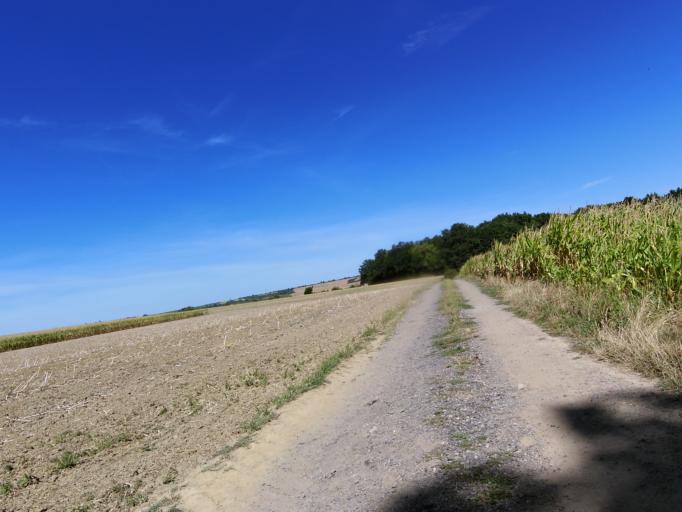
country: DE
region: Bavaria
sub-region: Regierungsbezirk Unterfranken
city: Theilheim
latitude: 49.7479
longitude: 10.0296
